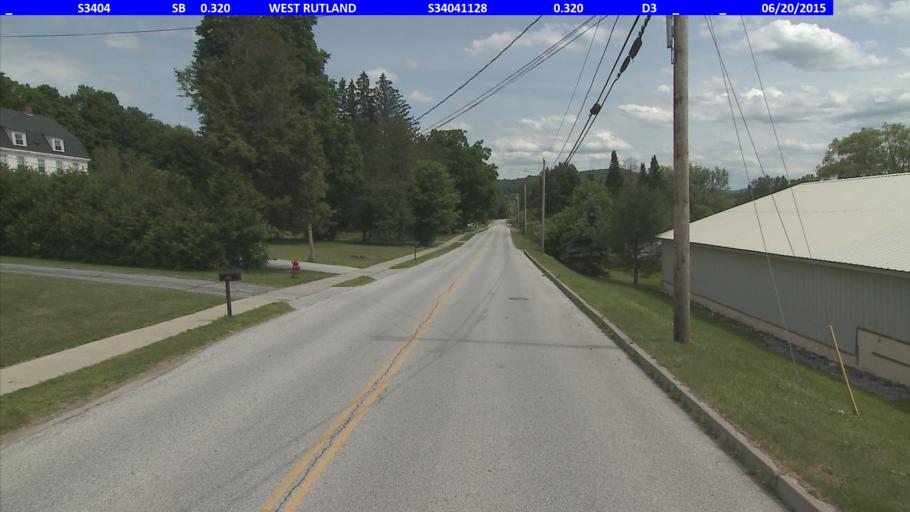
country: US
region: Vermont
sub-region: Rutland County
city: West Rutland
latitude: 43.5977
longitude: -73.0416
